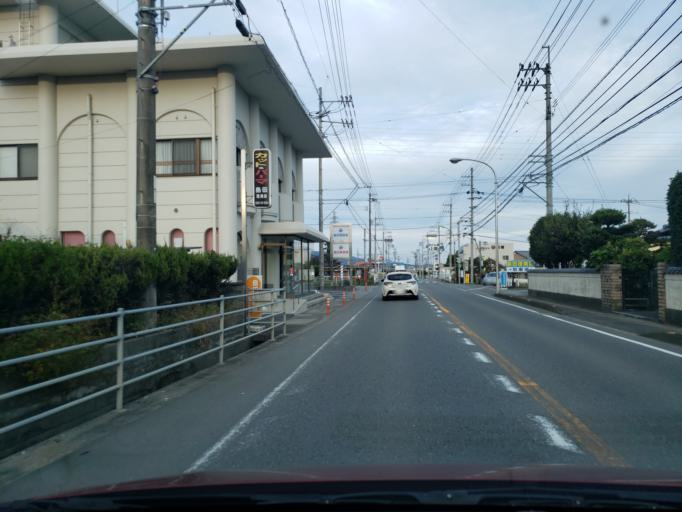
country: JP
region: Tokushima
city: Kamojimacho-jogejima
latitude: 34.0922
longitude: 134.3062
